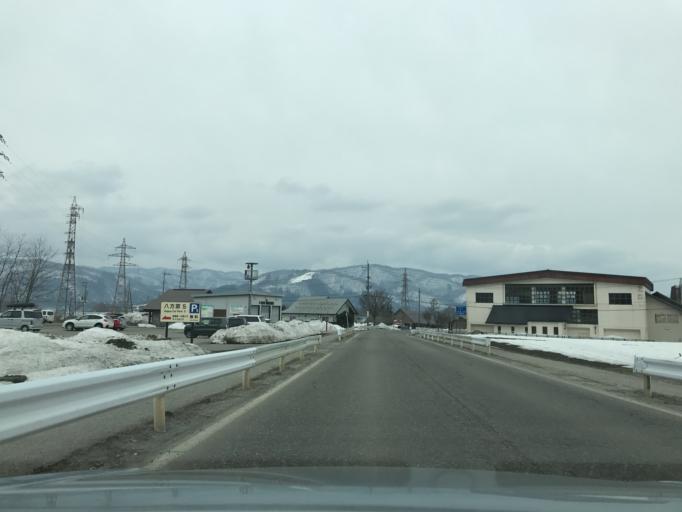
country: JP
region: Nagano
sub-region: Kitaazumi Gun
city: Hakuba
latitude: 36.7035
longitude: 137.8458
